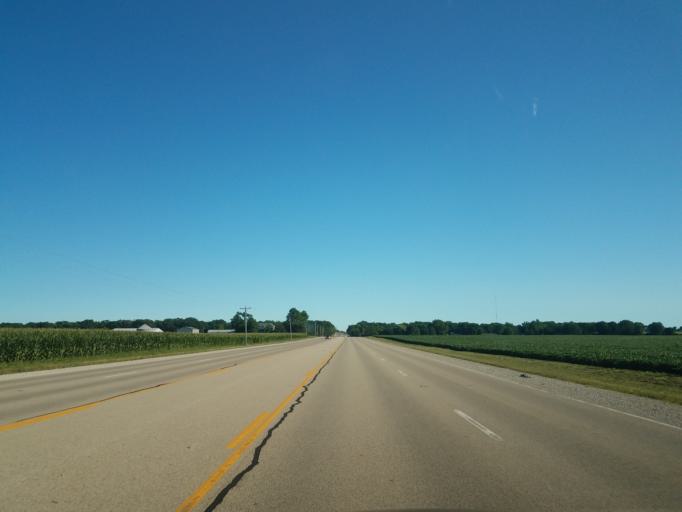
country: US
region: Illinois
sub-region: McLean County
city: Downs
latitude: 40.4318
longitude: -88.9015
